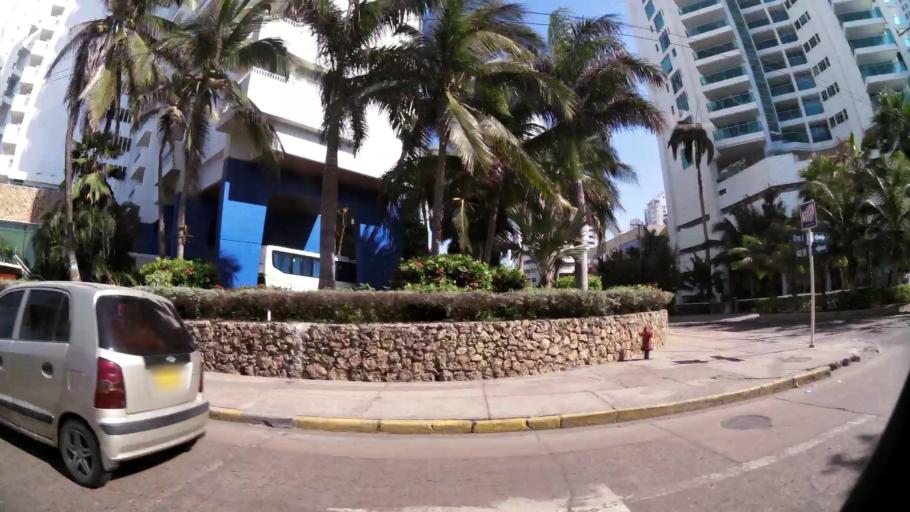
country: CO
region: Bolivar
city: Cartagena
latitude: 10.4076
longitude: -75.5529
